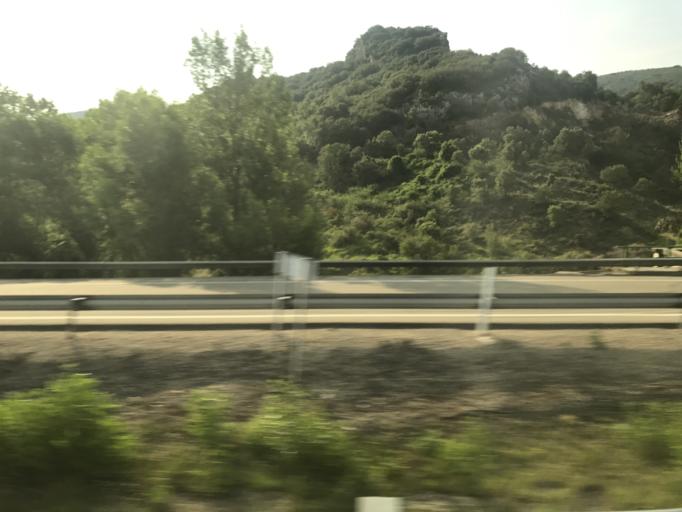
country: ES
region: Castille and Leon
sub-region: Provincia de Burgos
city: Ameyugo
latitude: 42.6485
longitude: -3.0808
